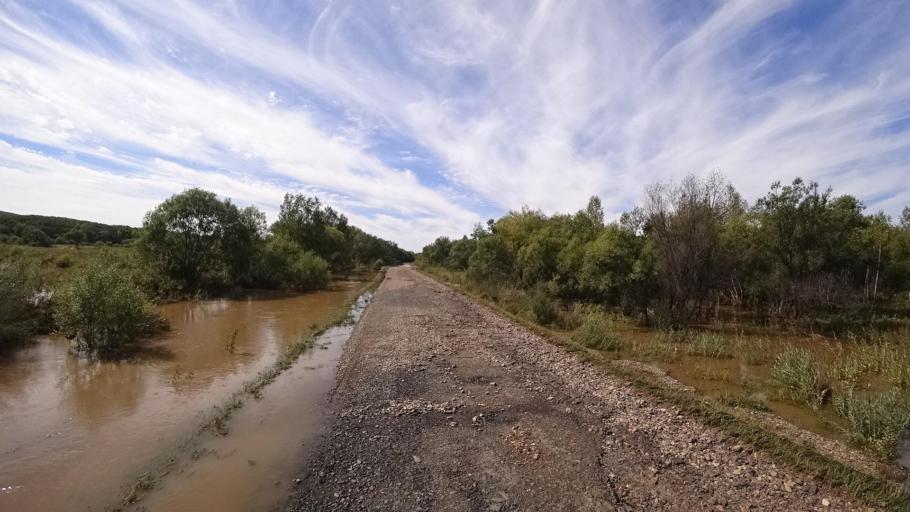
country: RU
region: Primorskiy
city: Kirovskiy
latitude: 44.7668
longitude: 133.6189
